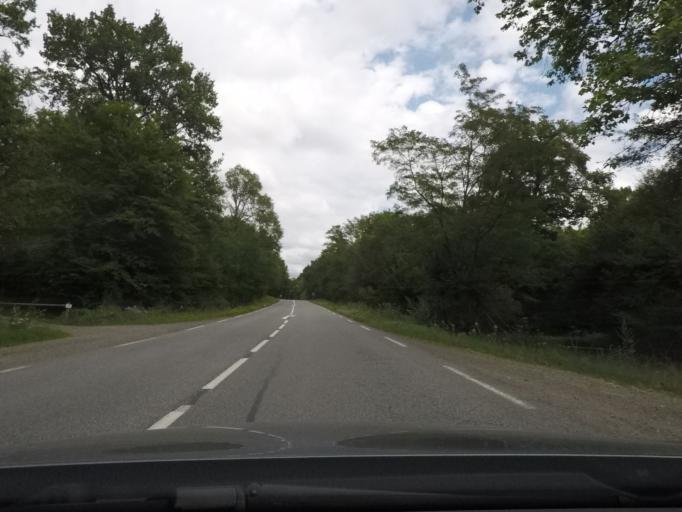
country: FR
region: Auvergne
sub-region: Departement du Puy-de-Dome
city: Randan
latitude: 46.0337
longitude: 3.3593
